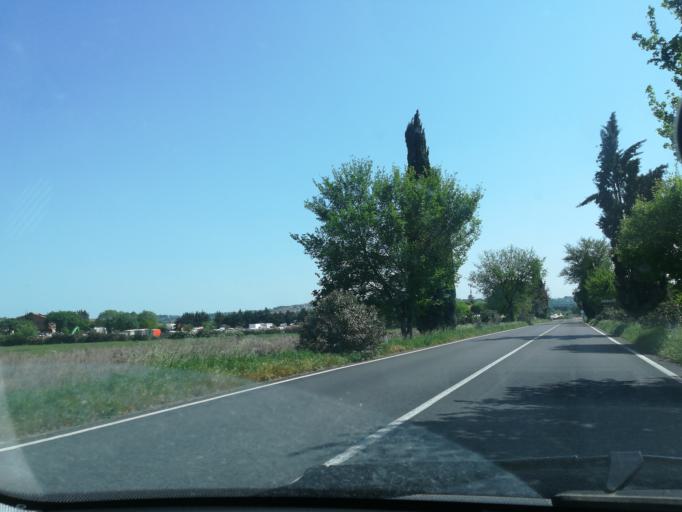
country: IT
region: The Marches
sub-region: Provincia di Macerata
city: Piediripa
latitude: 43.2779
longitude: 13.4856
